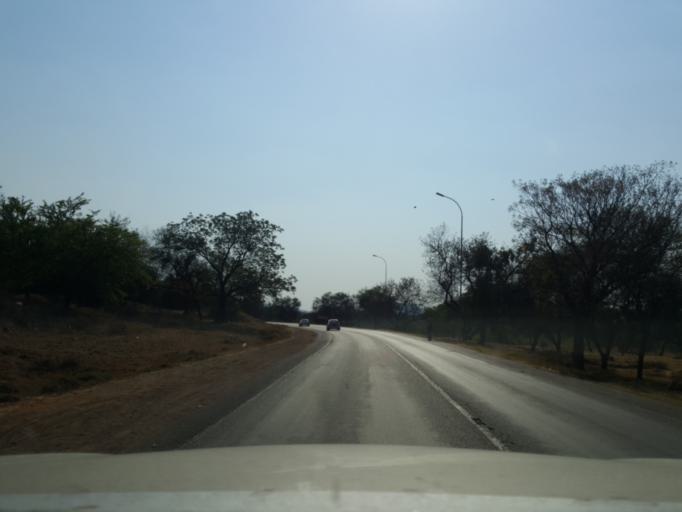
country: BW
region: South East
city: Lobatse
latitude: -25.2276
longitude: 25.6747
